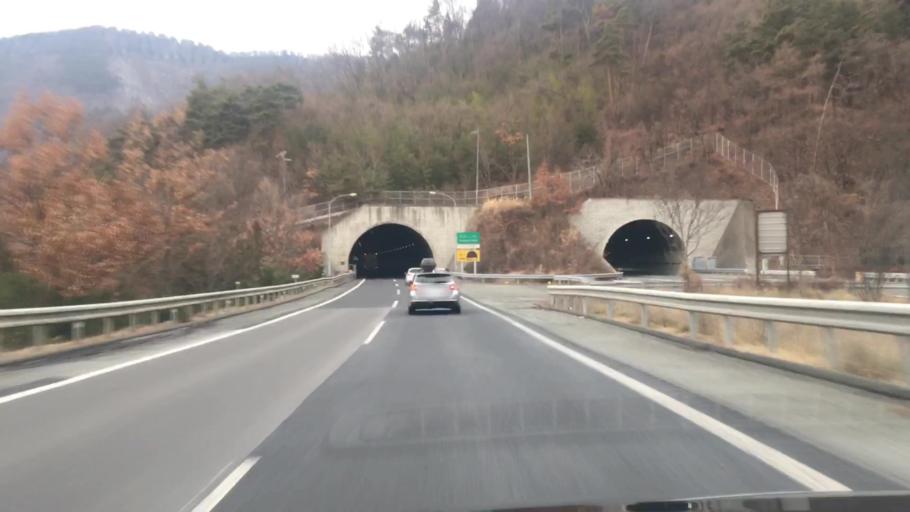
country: JP
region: Nagano
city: Ueda
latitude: 36.4735
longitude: 138.1963
